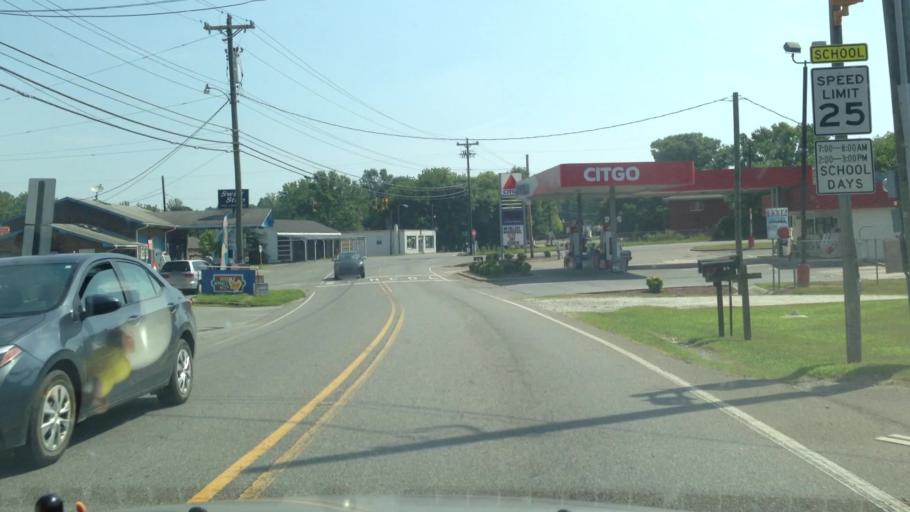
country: US
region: North Carolina
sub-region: Surry County
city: Flat Rock
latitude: 36.5115
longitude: -80.5708
